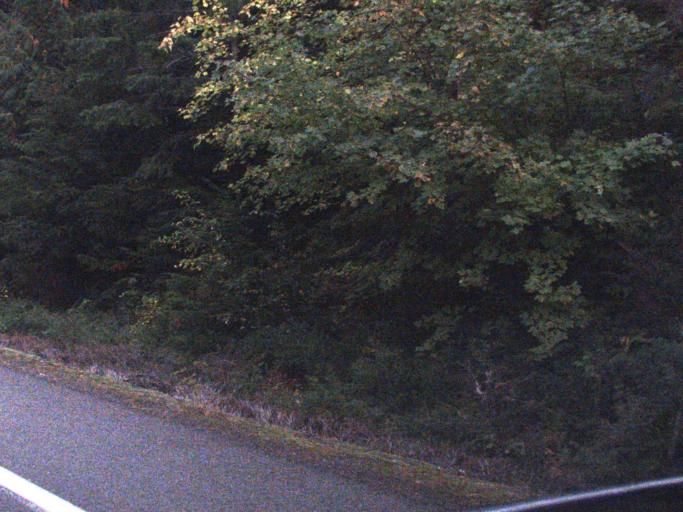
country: US
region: Washington
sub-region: Snohomish County
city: Darrington
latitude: 48.6917
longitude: -120.8925
